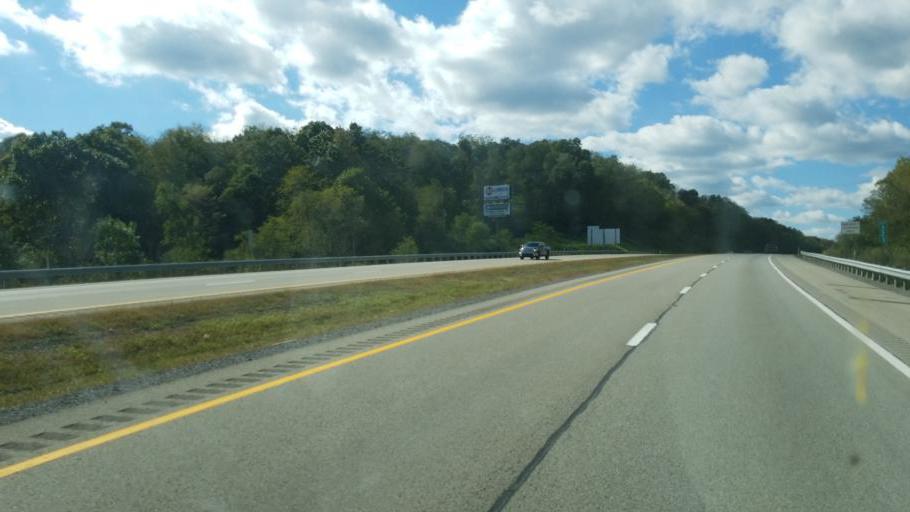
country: US
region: West Virginia
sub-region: Preston County
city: Kingwood
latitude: 39.6574
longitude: -79.6561
